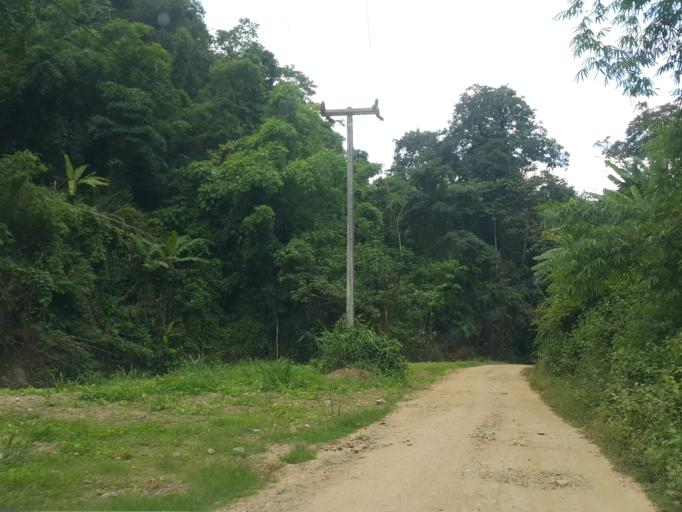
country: TH
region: Chiang Mai
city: Phrao
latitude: 19.3188
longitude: 99.1220
